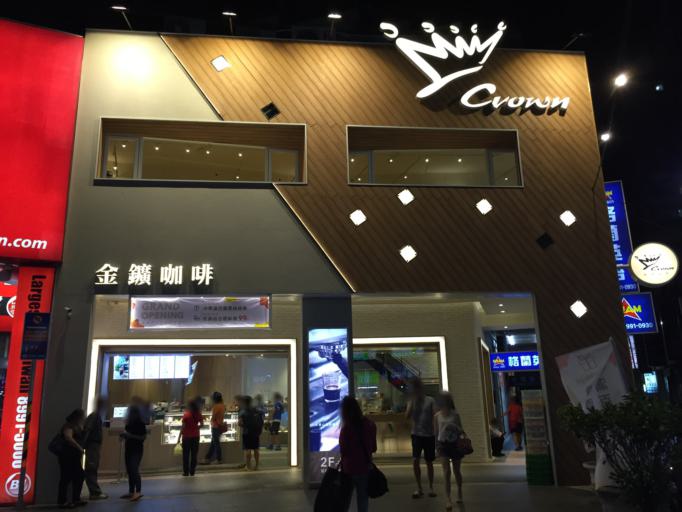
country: TW
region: Taipei
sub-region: Taipei
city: Banqiao
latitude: 25.0496
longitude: 121.4474
